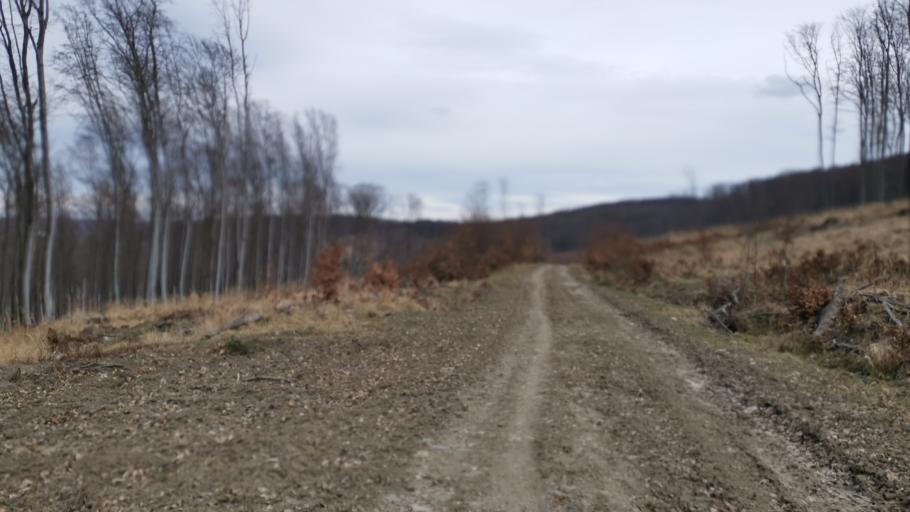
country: CZ
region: South Moravian
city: Knezdub
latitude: 48.8189
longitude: 17.3468
